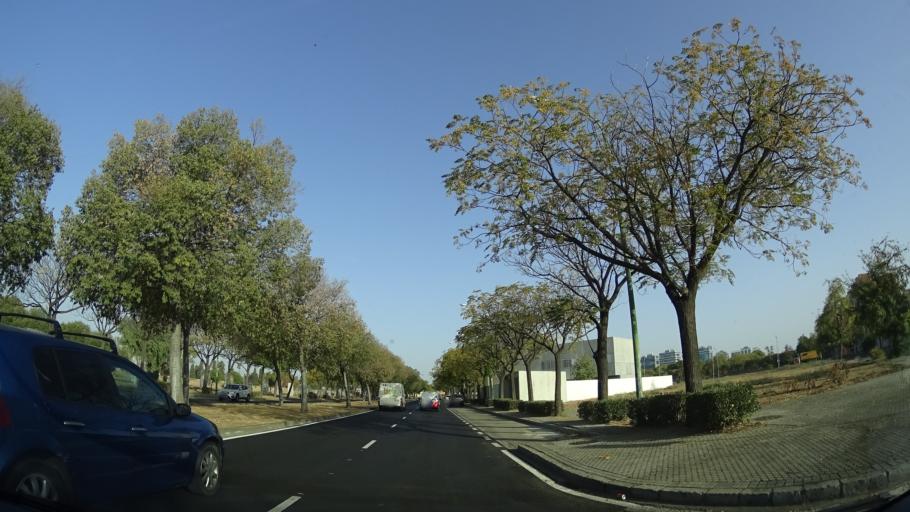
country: ES
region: Andalusia
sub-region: Provincia de Sevilla
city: Sevilla
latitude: 37.4180
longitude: -5.9754
